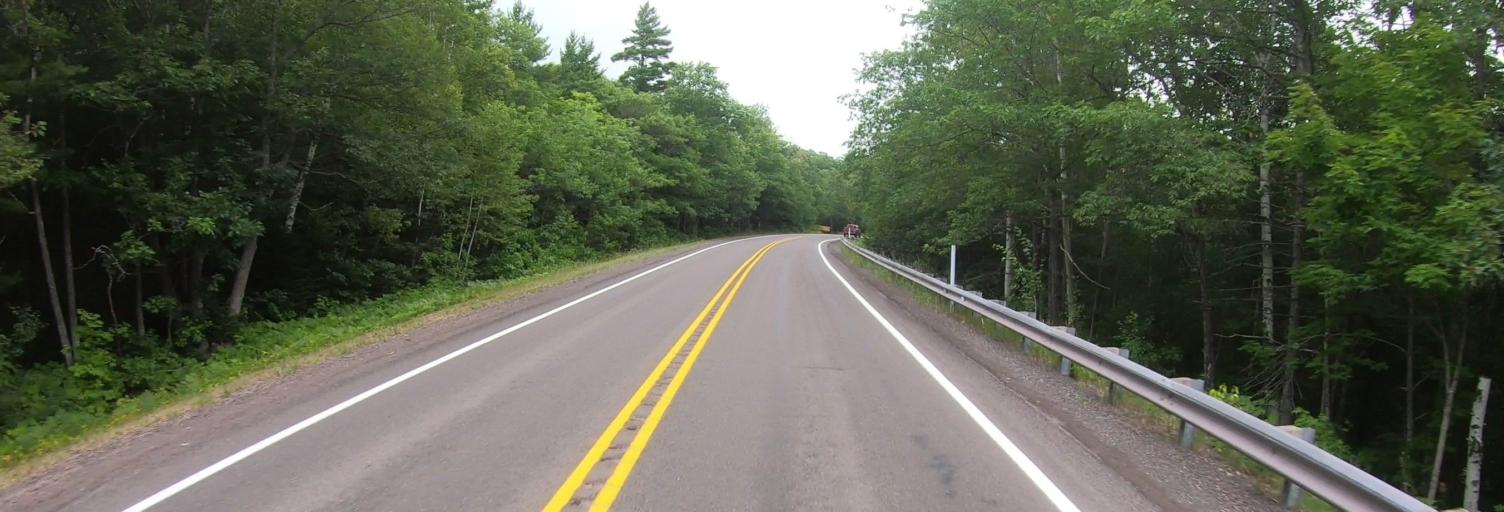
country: US
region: Michigan
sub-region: Keweenaw County
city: Eagle River
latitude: 47.4235
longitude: -88.0806
